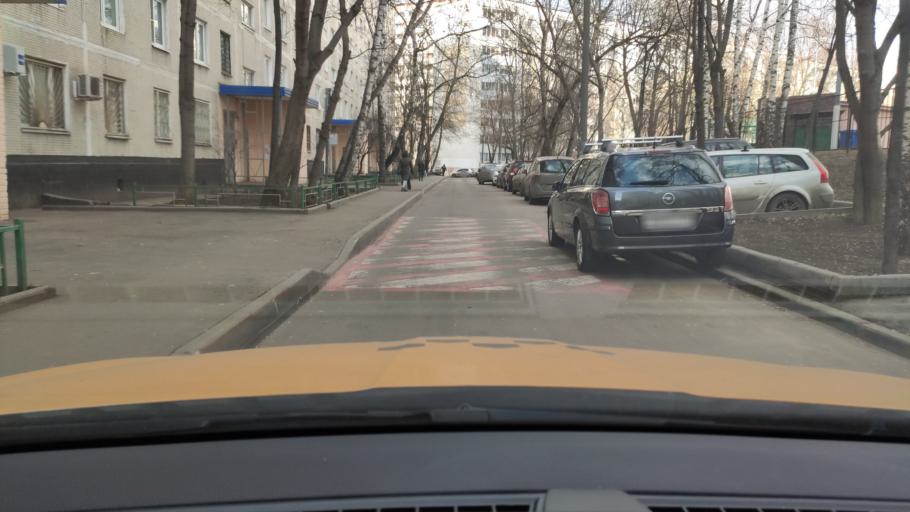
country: RU
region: Moscow
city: Orekhovo-Borisovo Severnoye
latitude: 55.6191
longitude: 37.6982
